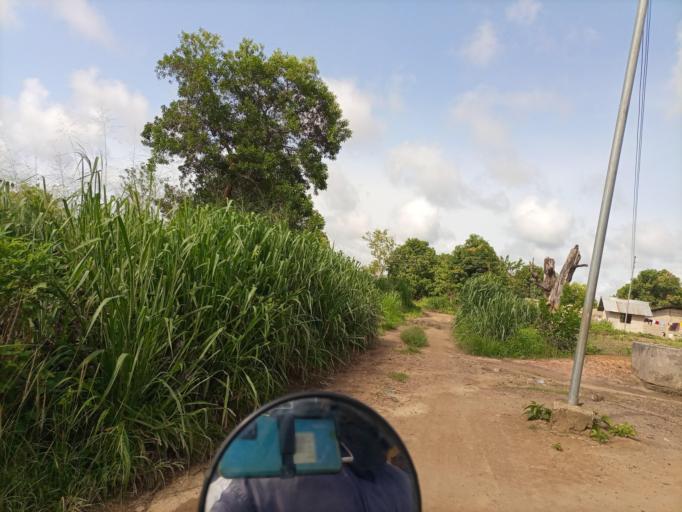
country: SL
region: Southern Province
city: Bo
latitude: 7.9625
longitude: -11.7649
